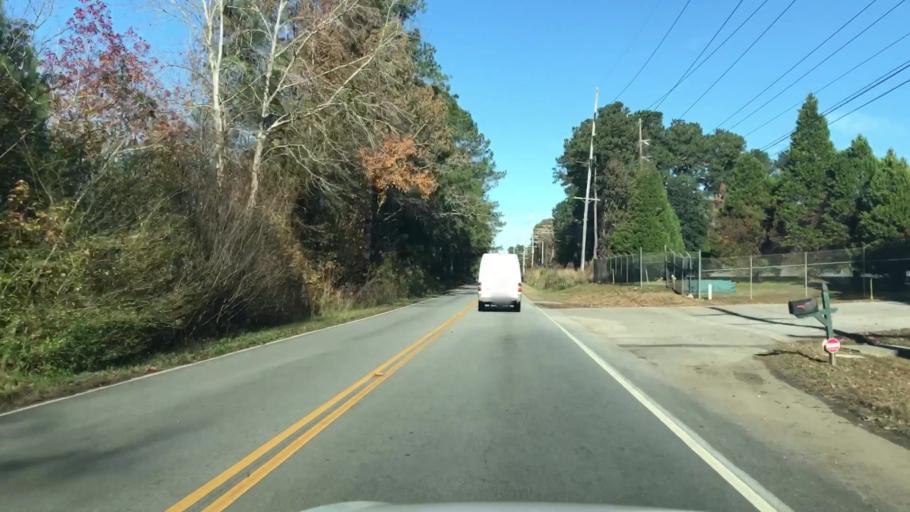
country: US
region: South Carolina
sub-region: Dorchester County
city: Centerville
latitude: 32.9855
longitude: -80.2201
